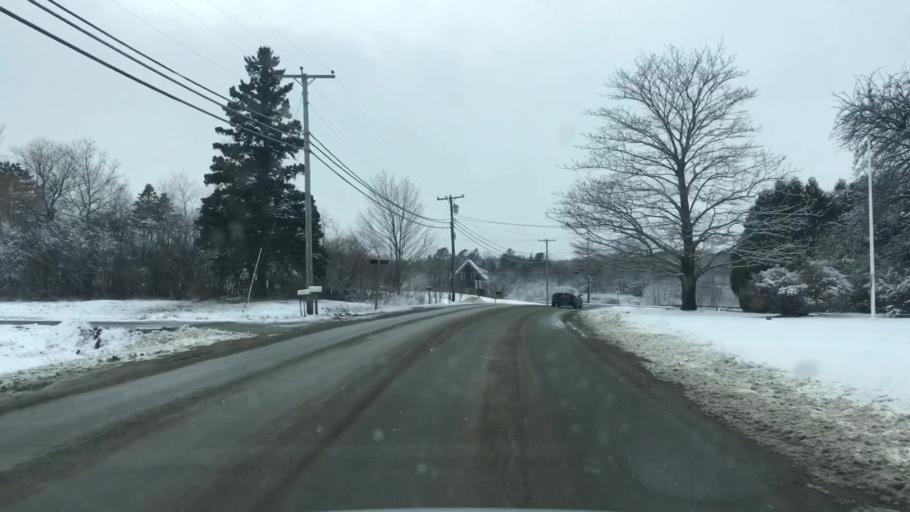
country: US
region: Maine
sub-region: Knox County
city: Rockland
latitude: 44.0766
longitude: -69.1031
